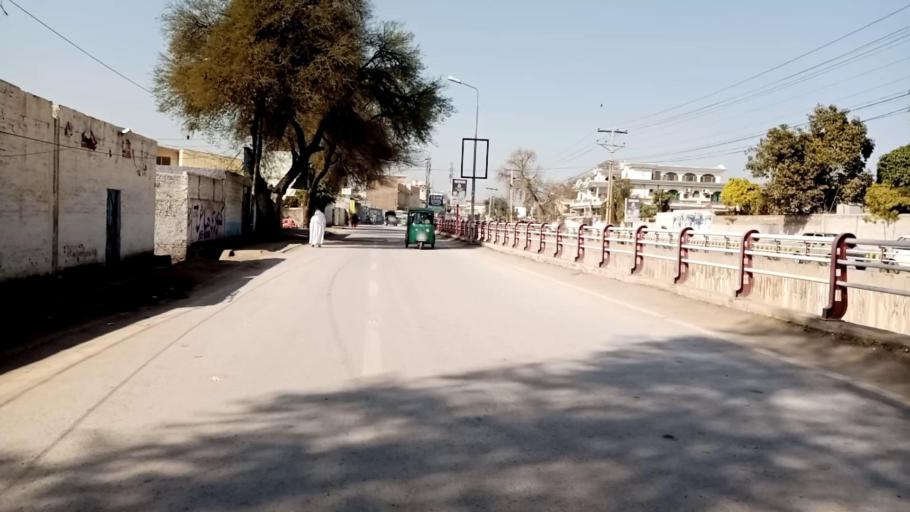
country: PK
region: Khyber Pakhtunkhwa
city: Peshawar
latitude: 33.9888
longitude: 71.4901
